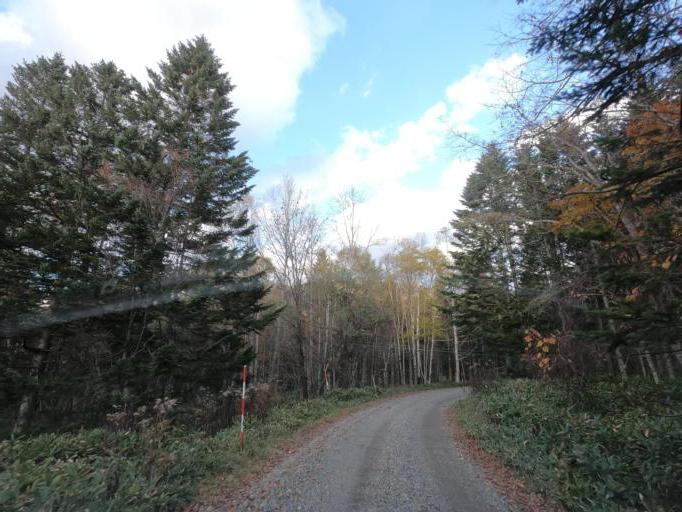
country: JP
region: Hokkaido
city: Otofuke
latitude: 43.4331
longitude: 143.1504
